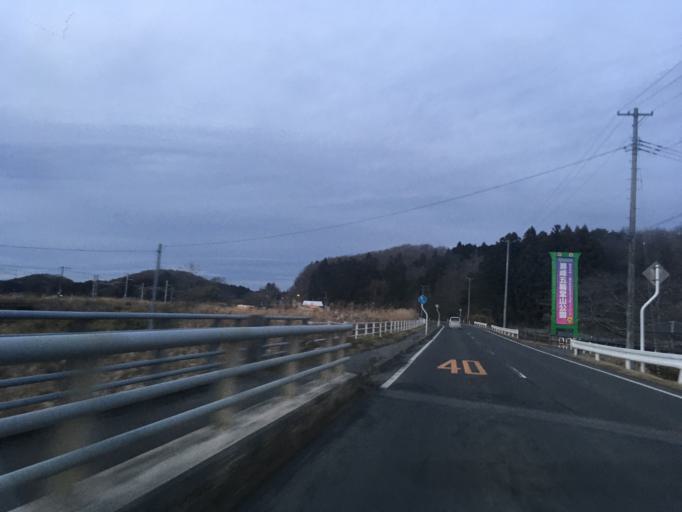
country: JP
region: Miyagi
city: Kogota
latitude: 38.6605
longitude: 141.0735
